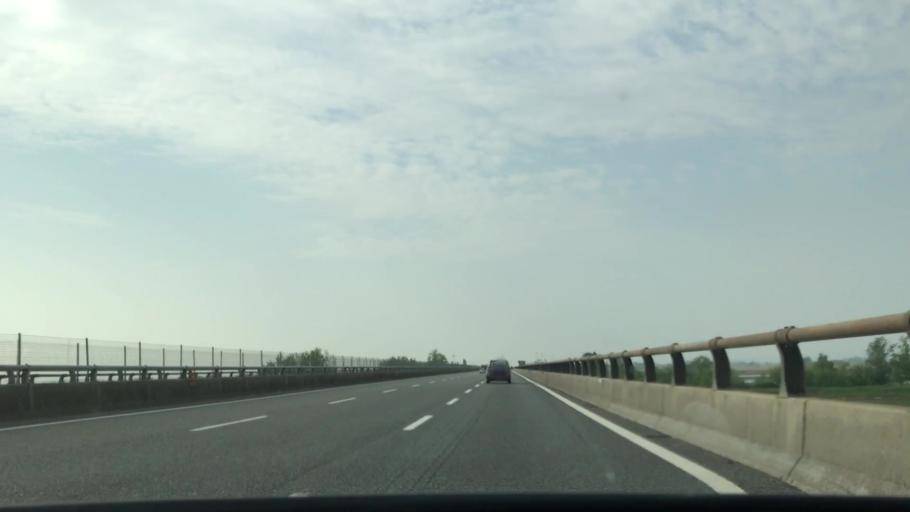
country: IT
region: Piedmont
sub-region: Provincia di Vercelli
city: Prarolo
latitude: 45.2986
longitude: 8.4707
